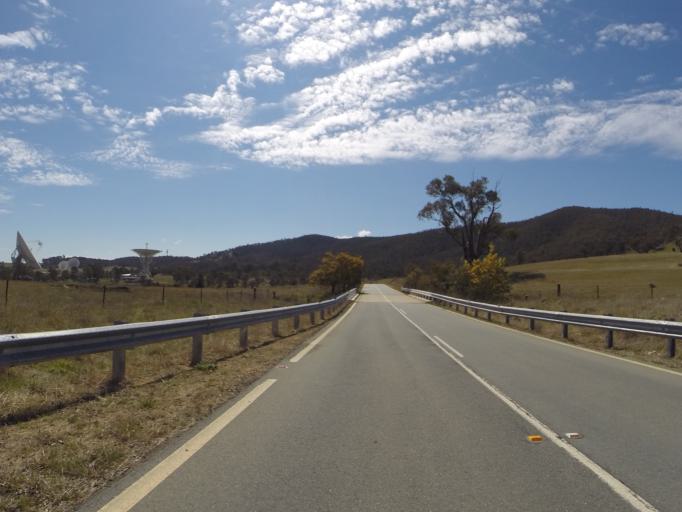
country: AU
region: Australian Capital Territory
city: Macarthur
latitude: -35.4086
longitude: 148.9825
